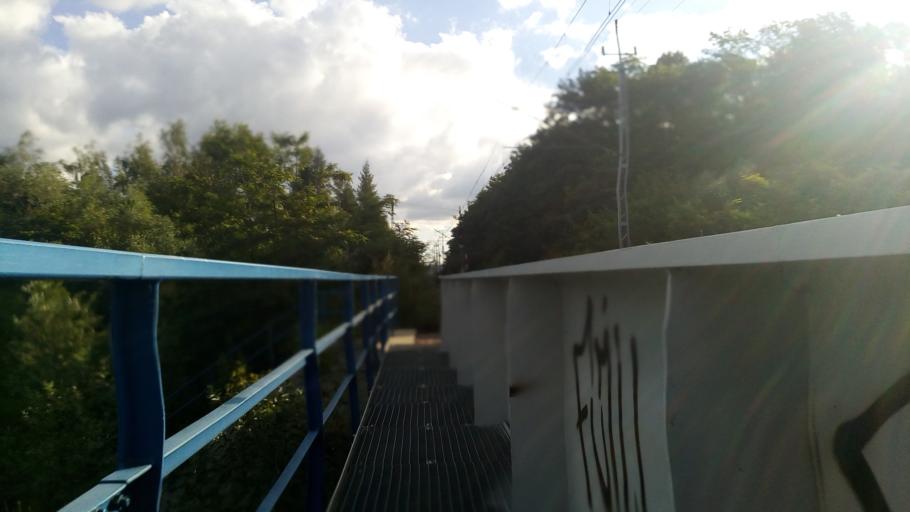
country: PL
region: Lesser Poland Voivodeship
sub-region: Powiat nowosadecki
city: Stary Sacz
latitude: 49.5779
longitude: 20.6525
